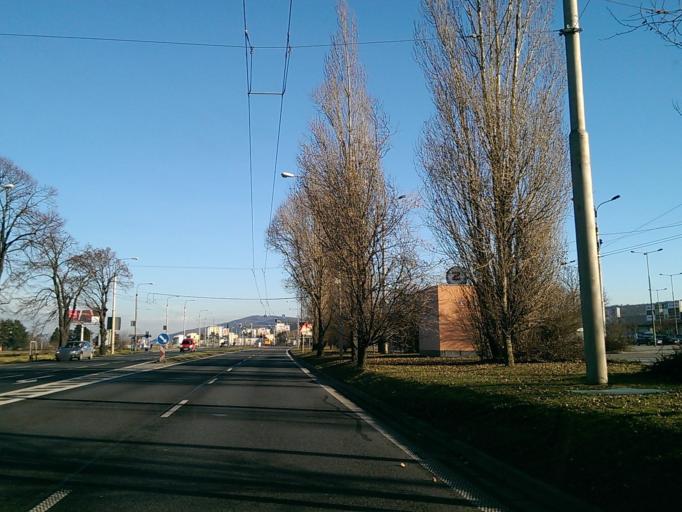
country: CZ
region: Zlin
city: Tecovice
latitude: 49.2050
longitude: 17.5690
